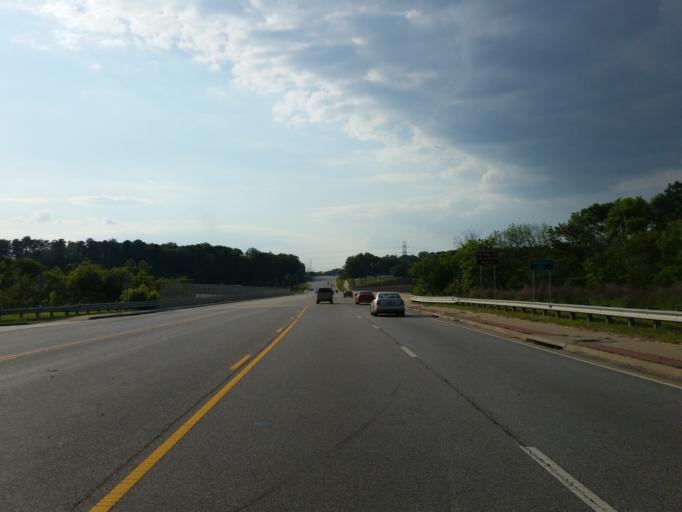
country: US
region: Georgia
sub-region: Cobb County
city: Vinings
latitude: 33.8163
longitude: -84.4787
